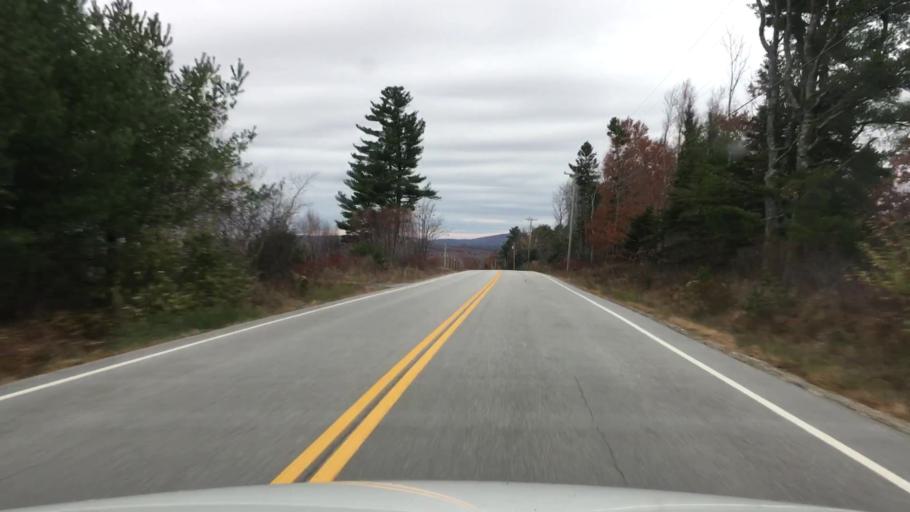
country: US
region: Maine
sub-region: Hancock County
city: Orland
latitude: 44.5469
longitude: -68.6889
